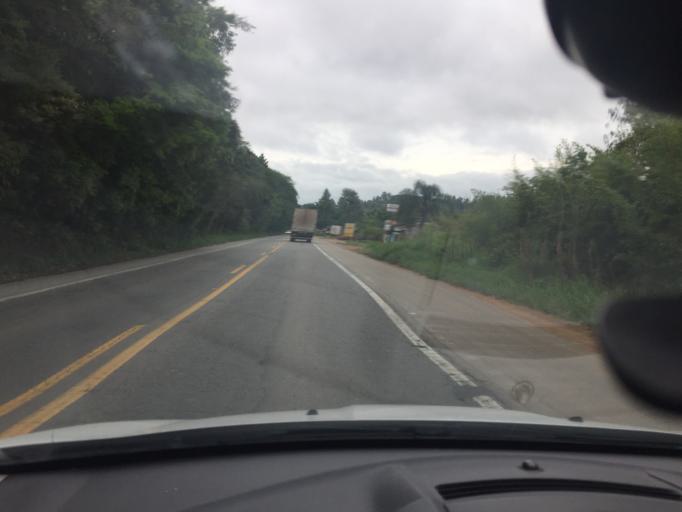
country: BR
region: Sao Paulo
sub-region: Jarinu
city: Jarinu
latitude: -23.1193
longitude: -46.7293
